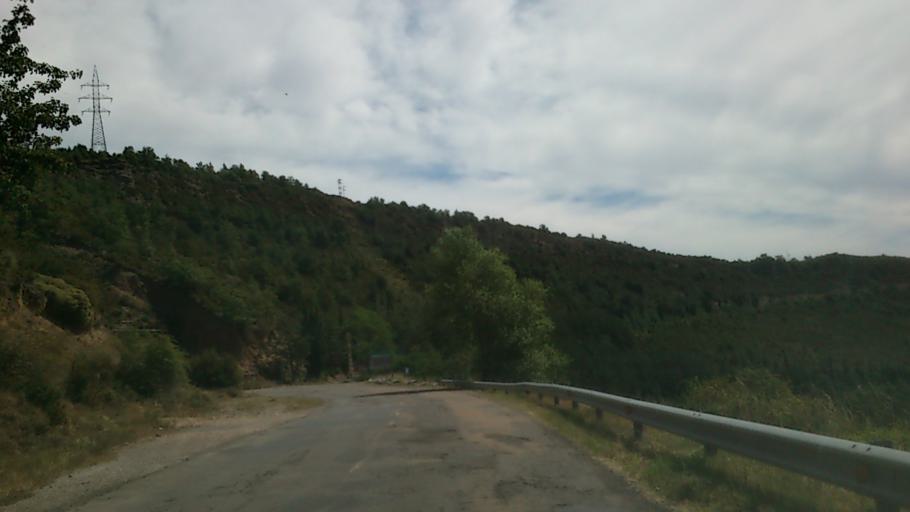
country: ES
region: Aragon
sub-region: Provincia de Huesca
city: Arguis
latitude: 42.3277
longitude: -0.4091
